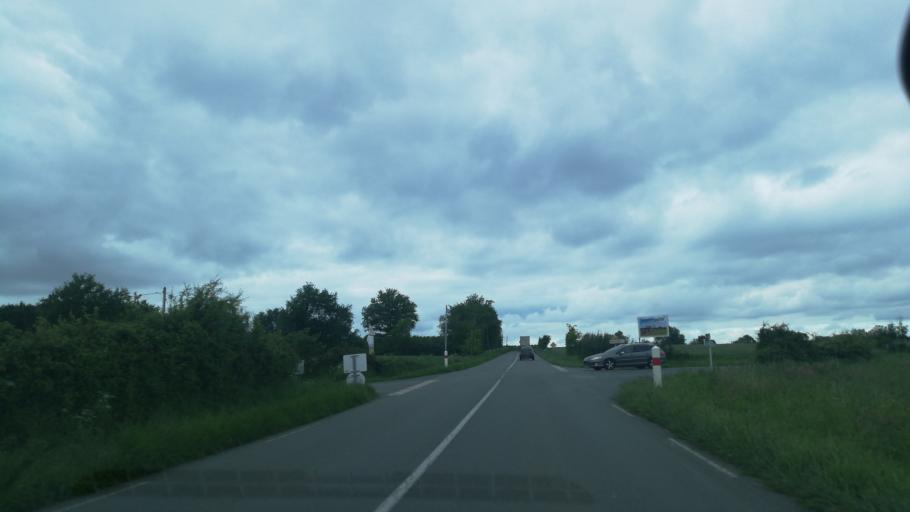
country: FR
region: Poitou-Charentes
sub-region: Departement des Deux-Sevres
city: La Chapelle-Saint-Laurent
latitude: 46.7598
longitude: -0.4732
